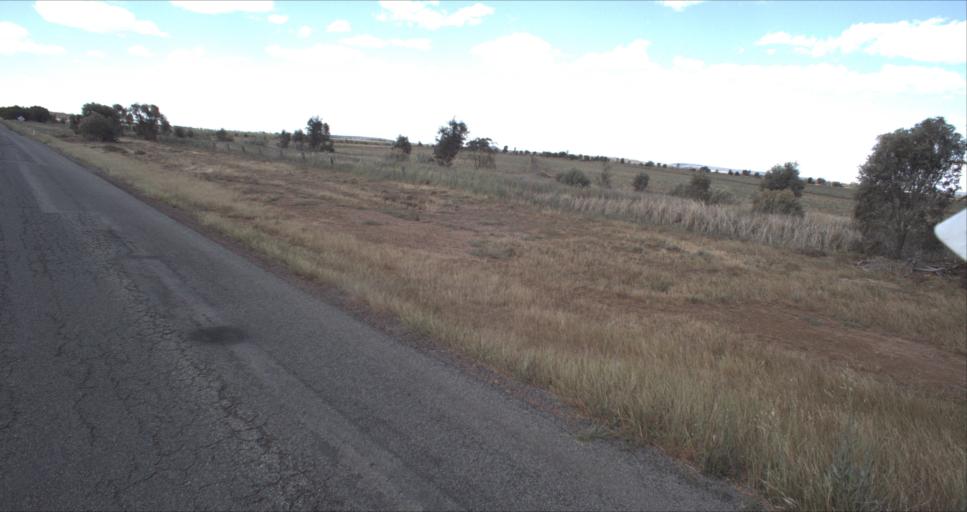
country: AU
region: New South Wales
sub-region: Leeton
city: Leeton
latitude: -34.4441
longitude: 146.2558
